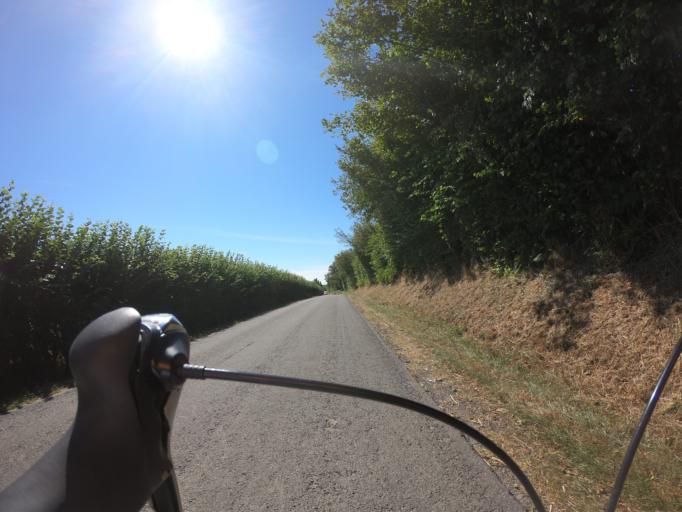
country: FR
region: Lower Normandy
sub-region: Departement de l'Orne
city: Saint-Denis-sur-Sarthon
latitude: 48.5238
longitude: -0.0879
